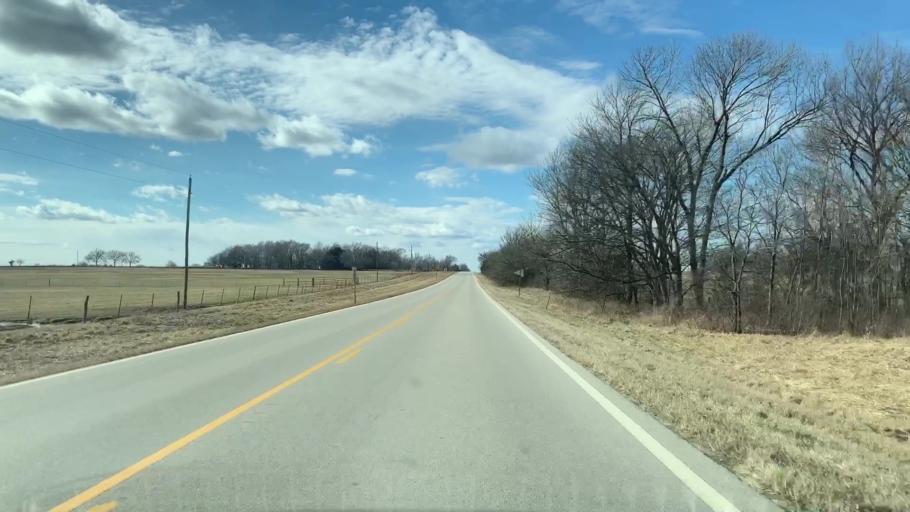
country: US
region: Kansas
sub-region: Neosho County
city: Chanute
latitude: 37.5288
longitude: -95.4383
